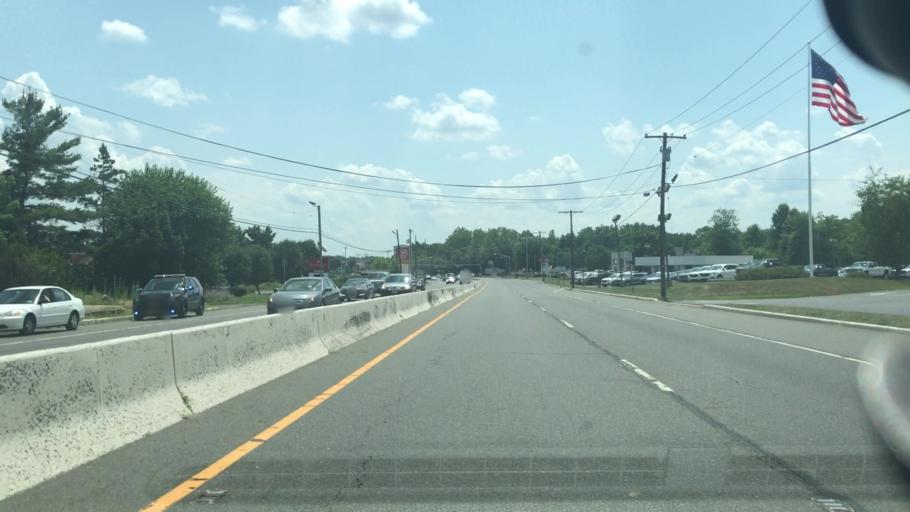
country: US
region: New Jersey
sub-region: Hunterdon County
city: Flemington
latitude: 40.4944
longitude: -74.8599
